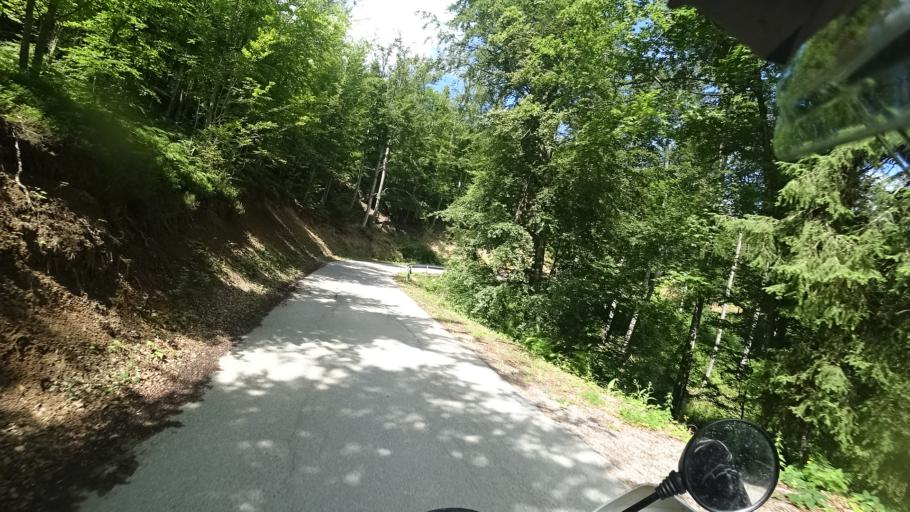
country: SI
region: Osilnica
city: Osilnica
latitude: 45.5143
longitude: 14.6672
